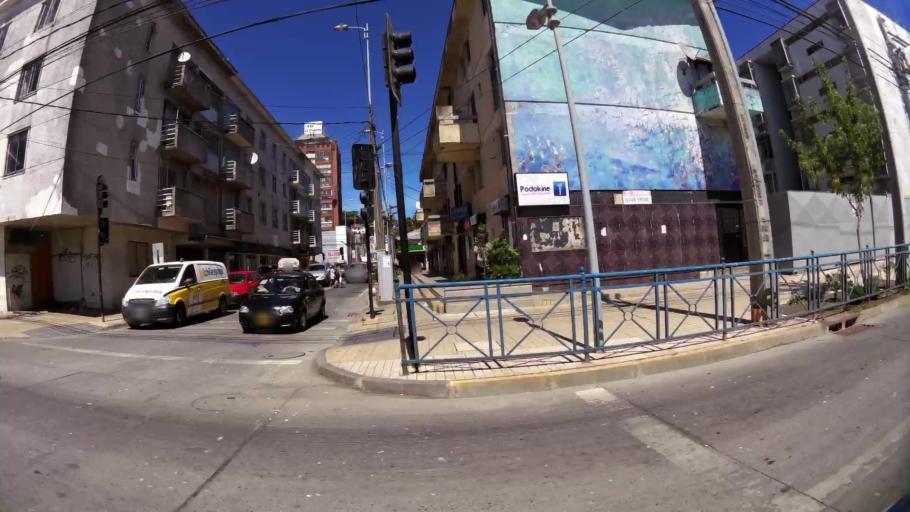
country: CL
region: Biobio
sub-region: Provincia de Concepcion
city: Talcahuano
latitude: -36.7133
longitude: -73.1124
